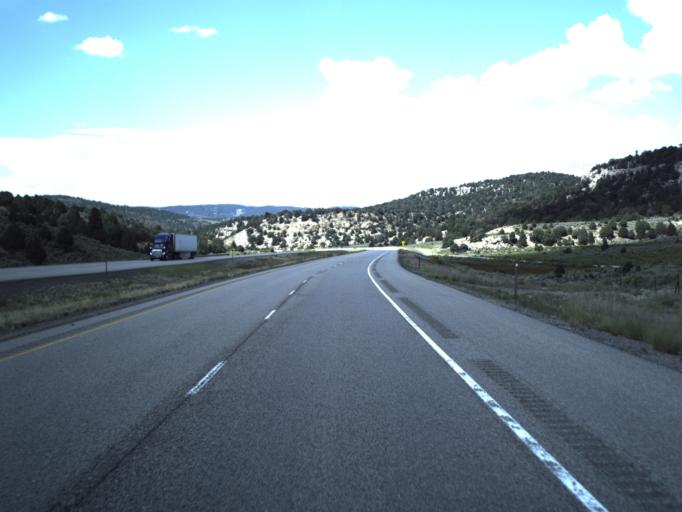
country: US
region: Utah
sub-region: Sevier County
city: Salina
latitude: 38.7973
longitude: -111.5108
